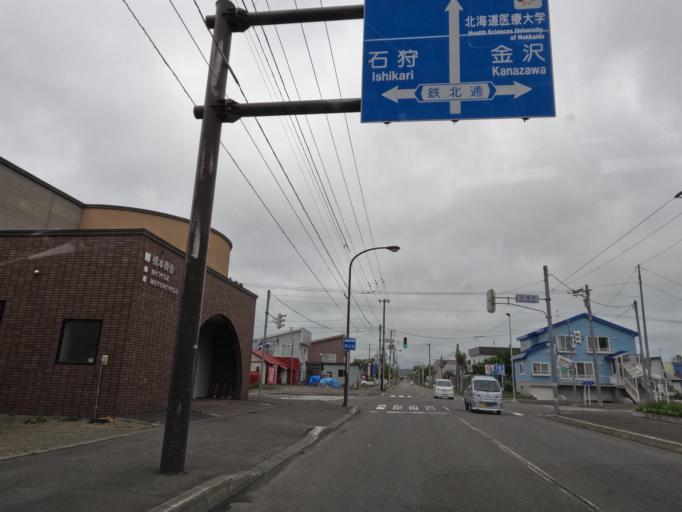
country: JP
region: Hokkaido
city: Tobetsu
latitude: 43.2252
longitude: 141.5177
